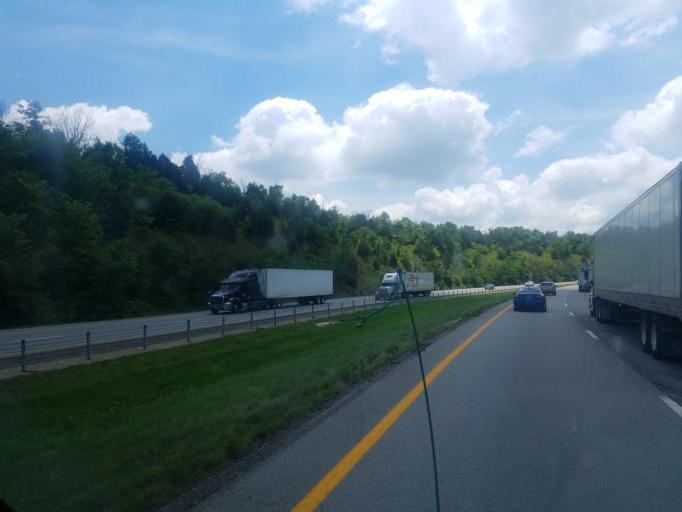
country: US
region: Kentucky
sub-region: Trimble County
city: Providence
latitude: 38.5882
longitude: -85.1755
